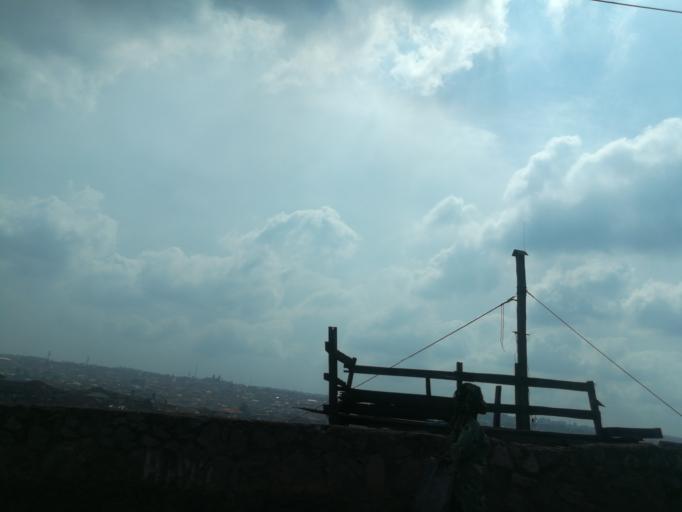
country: NG
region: Oyo
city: Ibadan
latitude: 7.3803
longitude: 3.8996
